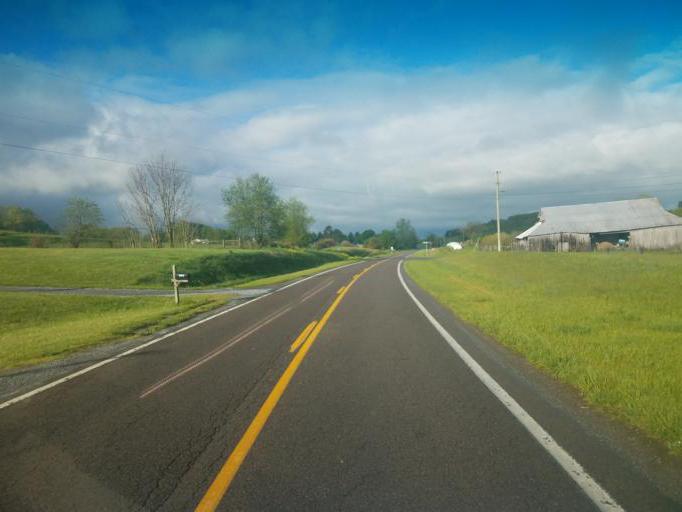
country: US
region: Virginia
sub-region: Washington County
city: Emory
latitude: 36.6892
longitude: -81.8076
